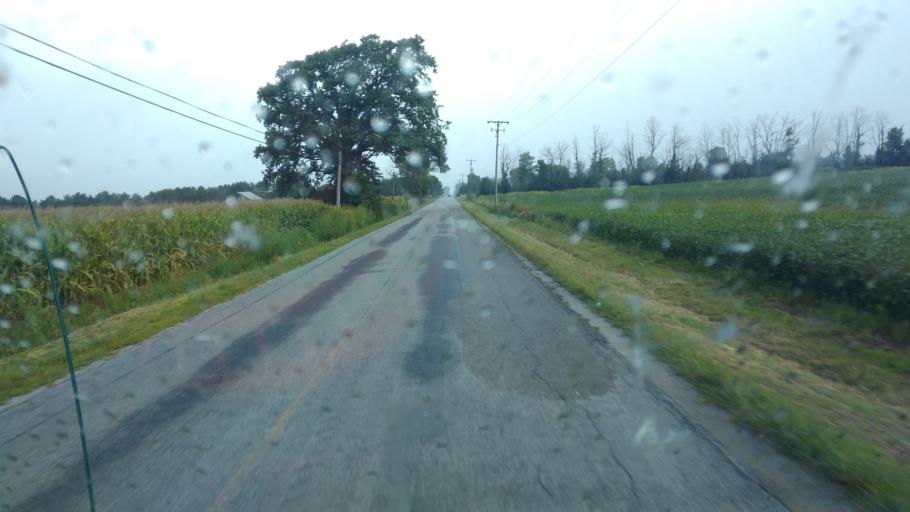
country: US
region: Ohio
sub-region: Hardin County
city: Kenton
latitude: 40.6719
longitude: -83.5380
